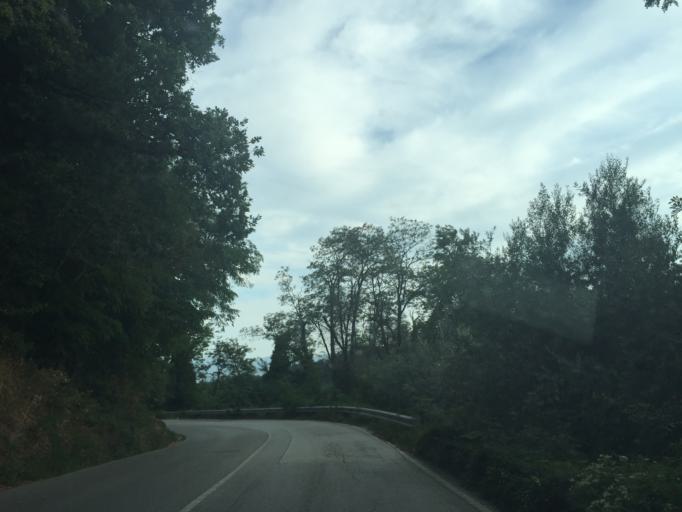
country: IT
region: Tuscany
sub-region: Provincia di Pistoia
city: Campo Tizzoro
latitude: 43.9813
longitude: 10.8634
